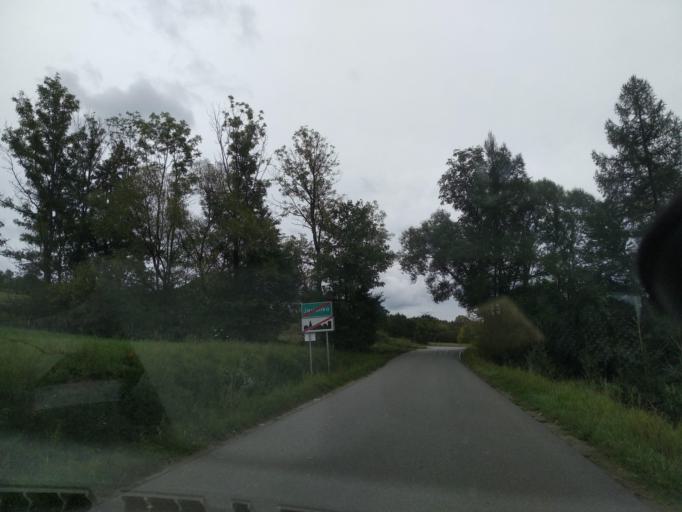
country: PL
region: Subcarpathian Voivodeship
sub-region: Powiat krosnienski
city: Iwonicz-Zdroj
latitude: 49.5422
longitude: 21.7394
